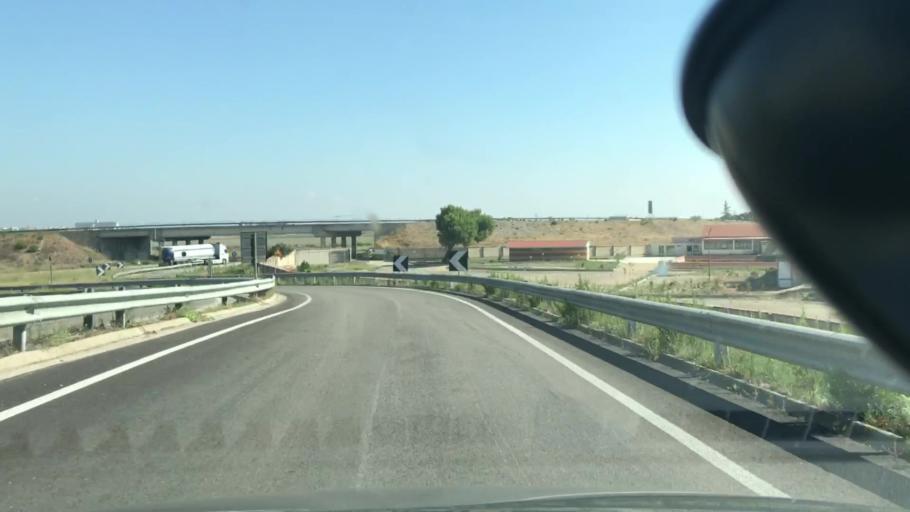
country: IT
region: Apulia
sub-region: Provincia di Foggia
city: Foggia
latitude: 41.4248
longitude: 15.5602
